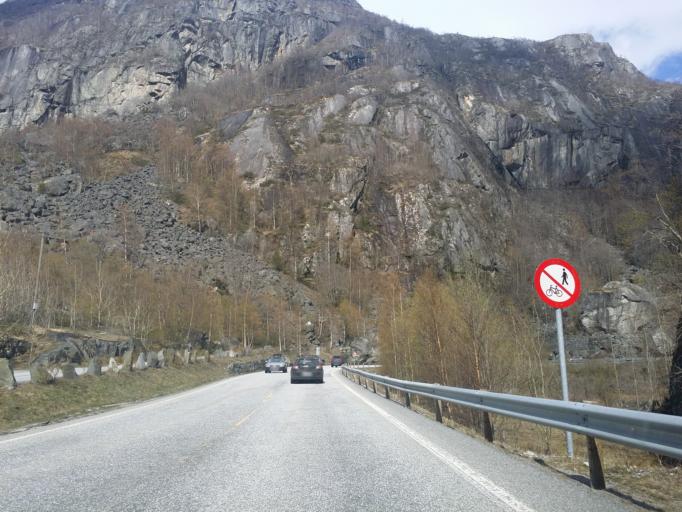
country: NO
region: Hordaland
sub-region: Eidfjord
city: Eidfjord
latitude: 60.4173
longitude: 7.1952
